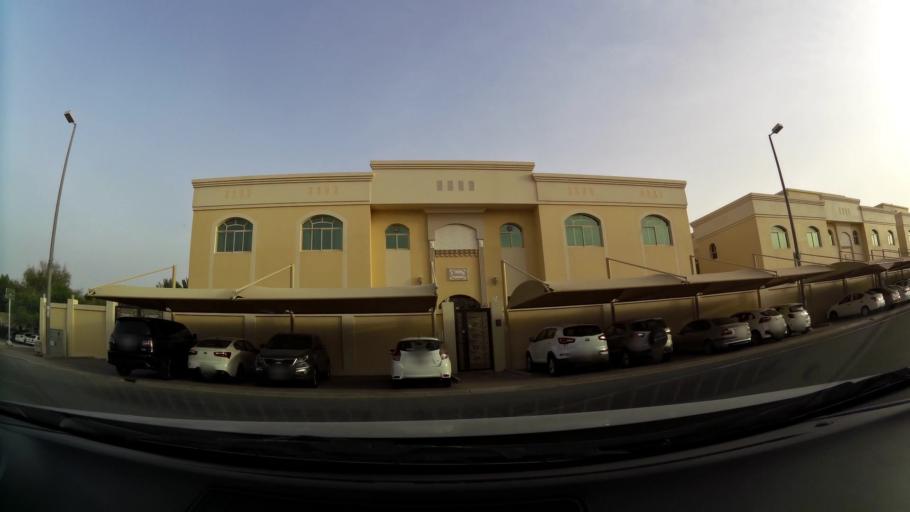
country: OM
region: Al Buraimi
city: Al Buraymi
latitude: 24.2450
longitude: 55.7341
